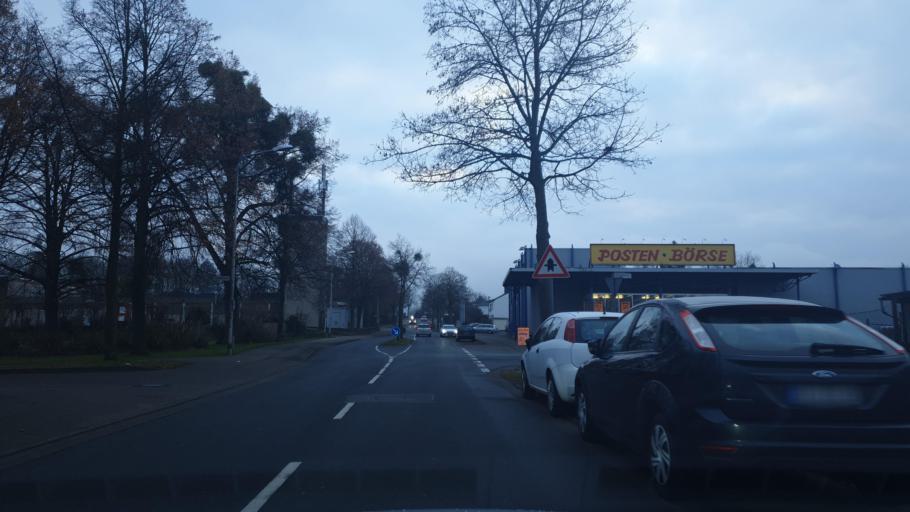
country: DE
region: Lower Saxony
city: Buckeburg
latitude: 52.2626
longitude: 9.0333
